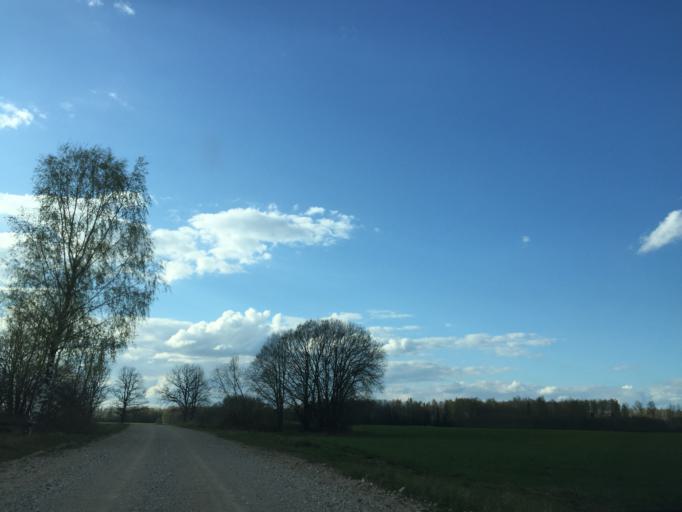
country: LV
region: Raunas
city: Rauna
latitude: 57.3679
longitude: 25.5107
